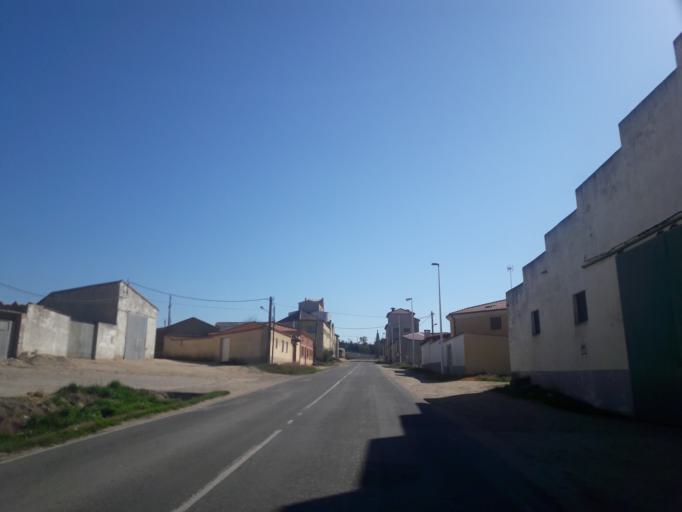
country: ES
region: Castille and Leon
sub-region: Provincia de Salamanca
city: Macotera
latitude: 40.8334
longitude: -5.2856
